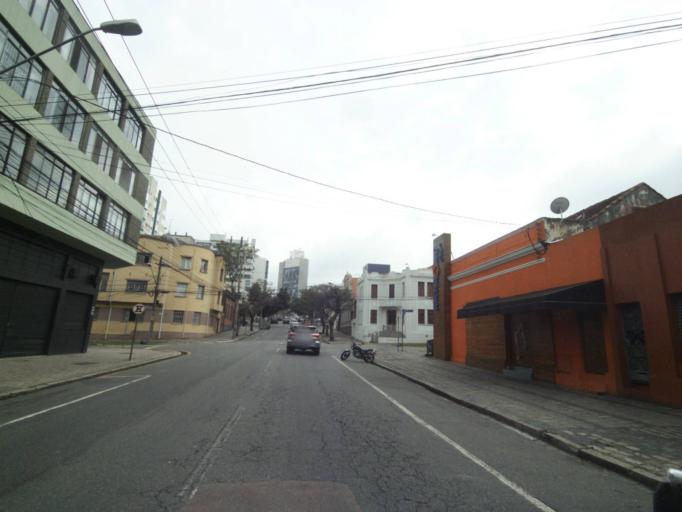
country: BR
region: Parana
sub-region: Curitiba
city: Curitiba
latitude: -25.4286
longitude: -49.2785
